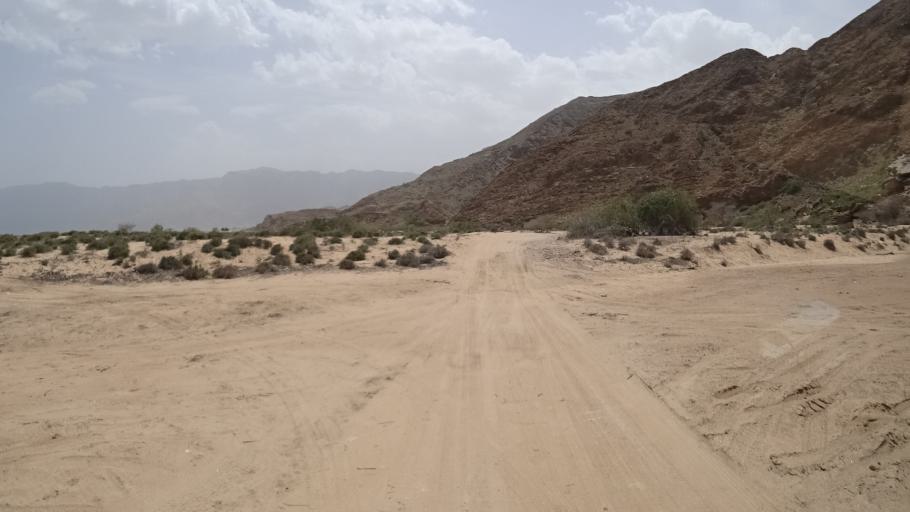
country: OM
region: Muhafazat Masqat
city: Muscat
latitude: 23.4481
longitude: 58.7797
